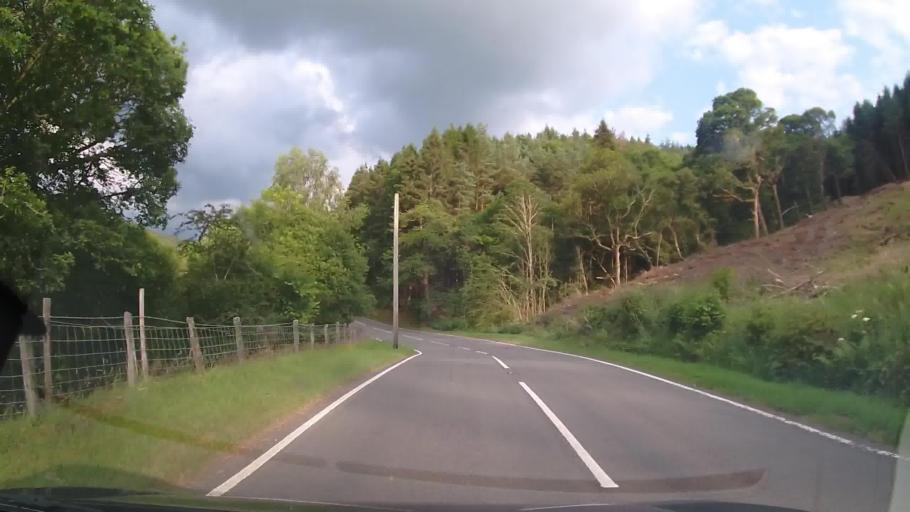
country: GB
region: Wales
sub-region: Gwynedd
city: Bala
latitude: 52.9060
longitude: -3.5308
